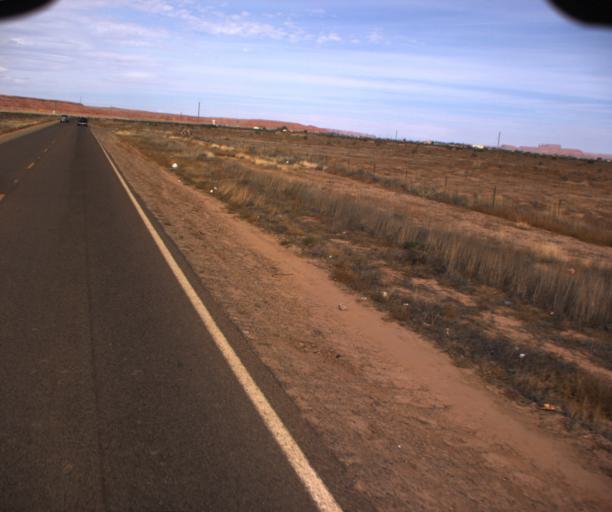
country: US
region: Arizona
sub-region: Apache County
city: Many Farms
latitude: 36.3301
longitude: -109.6216
